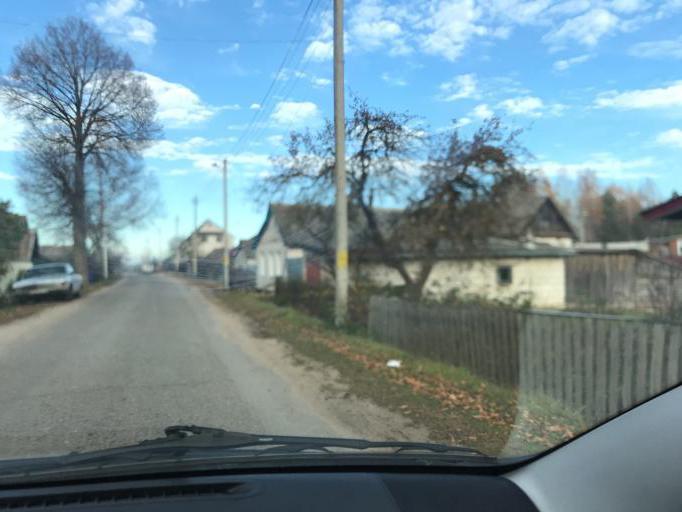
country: BY
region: Vitebsk
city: Haradok
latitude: 55.4579
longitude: 30.0100
